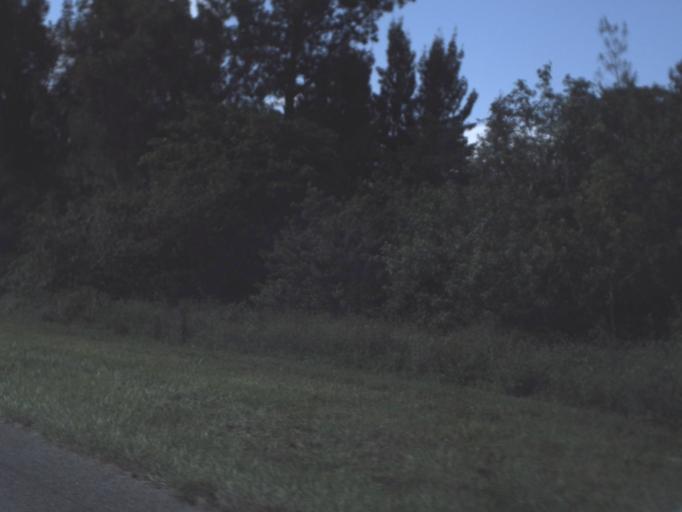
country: US
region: Florida
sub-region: Hendry County
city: Clewiston
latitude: 26.7534
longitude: -80.9079
